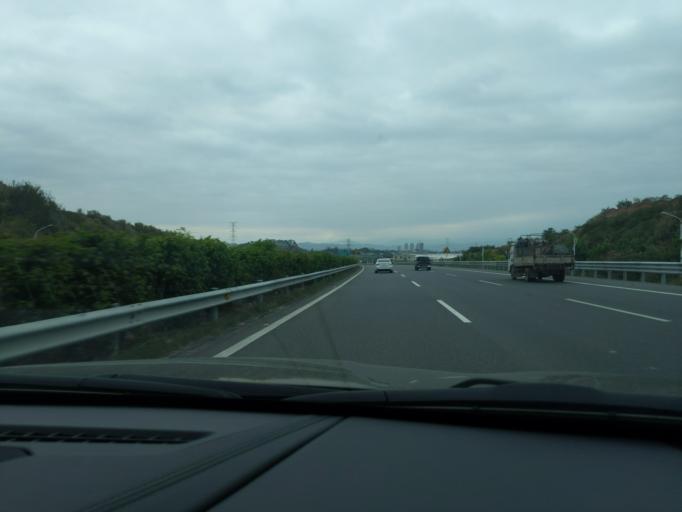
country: CN
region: Fujian
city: Neikeng
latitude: 24.7835
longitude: 118.4985
